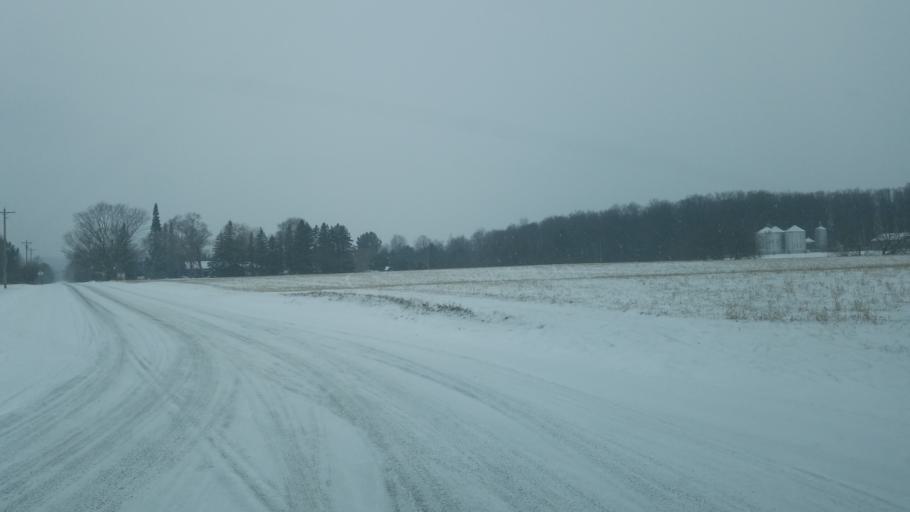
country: US
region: Michigan
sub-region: Osceola County
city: Reed City
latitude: 43.8218
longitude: -85.4041
